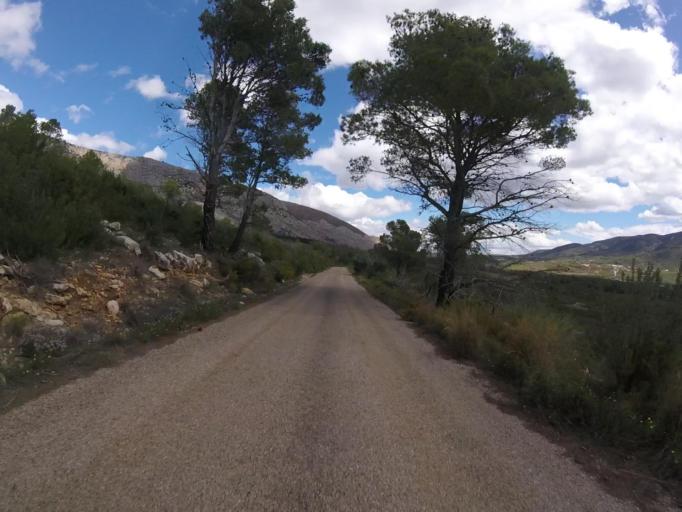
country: ES
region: Valencia
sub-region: Provincia de Castello
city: Sierra-Engarceran
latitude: 40.2840
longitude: -0.0700
